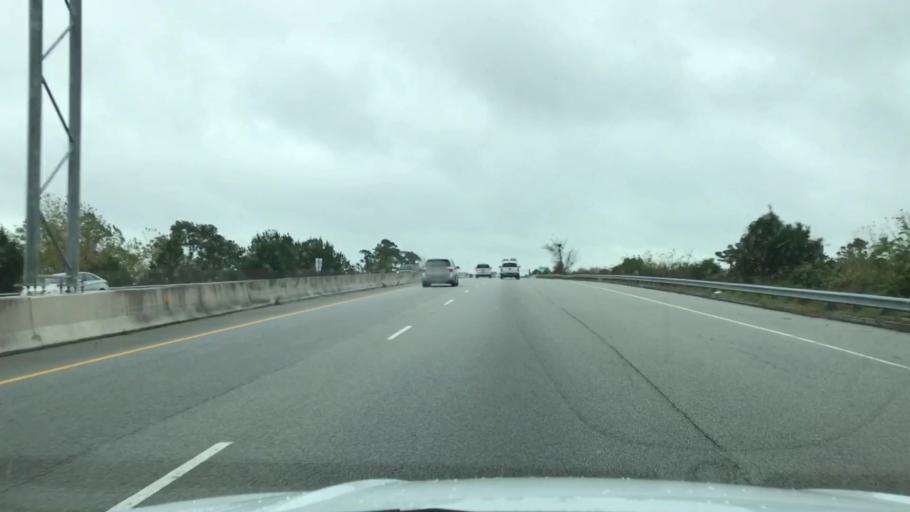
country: US
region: South Carolina
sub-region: Horry County
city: Myrtle Beach
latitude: 33.7515
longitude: -78.8507
